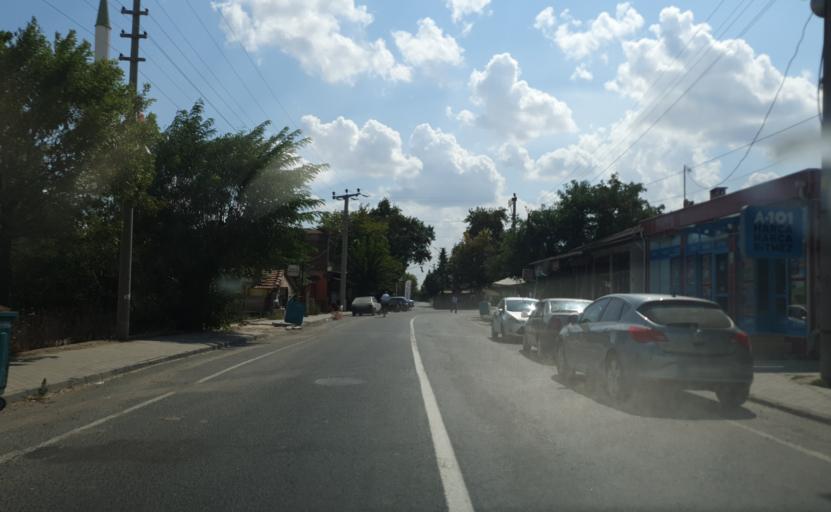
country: TR
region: Kirklareli
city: Luleburgaz
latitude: 41.3577
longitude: 27.3348
